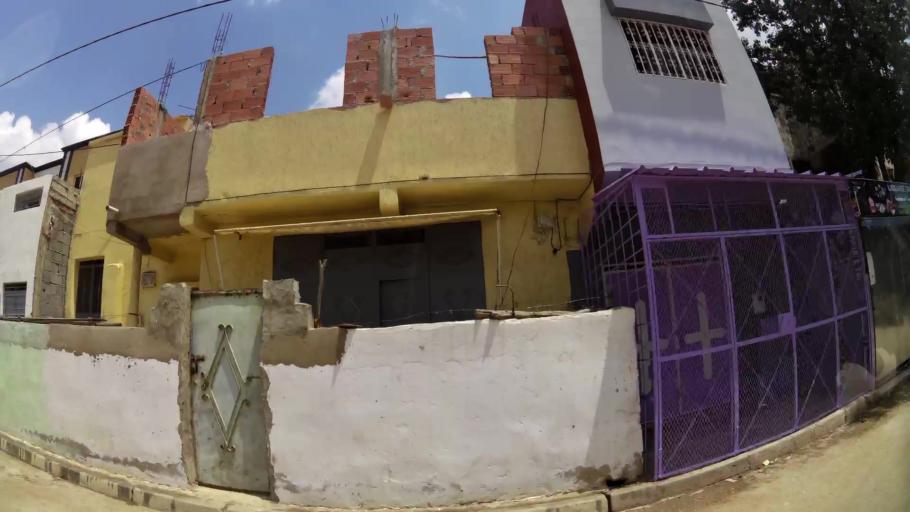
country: MA
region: Rabat-Sale-Zemmour-Zaer
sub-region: Khemisset
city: Tiflet
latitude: 34.0010
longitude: -6.5317
